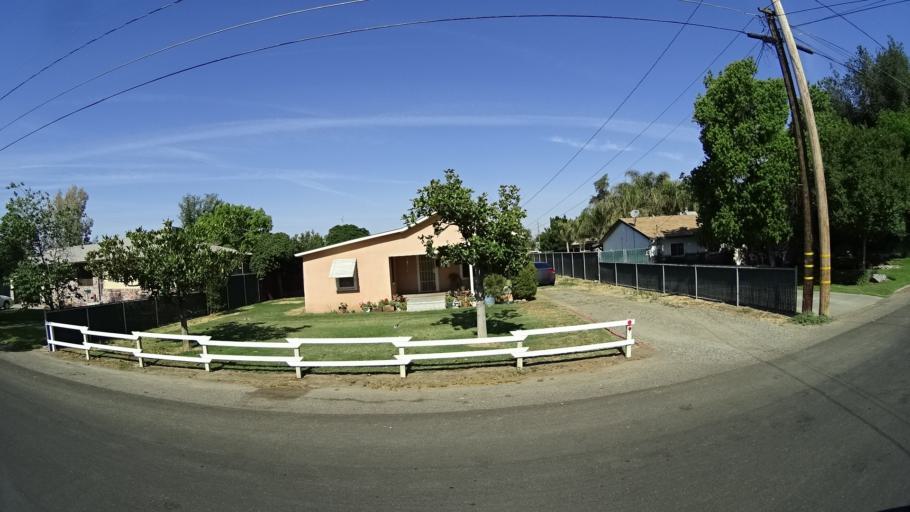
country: US
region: California
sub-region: Kings County
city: Hanford
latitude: 36.3389
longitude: -119.6350
